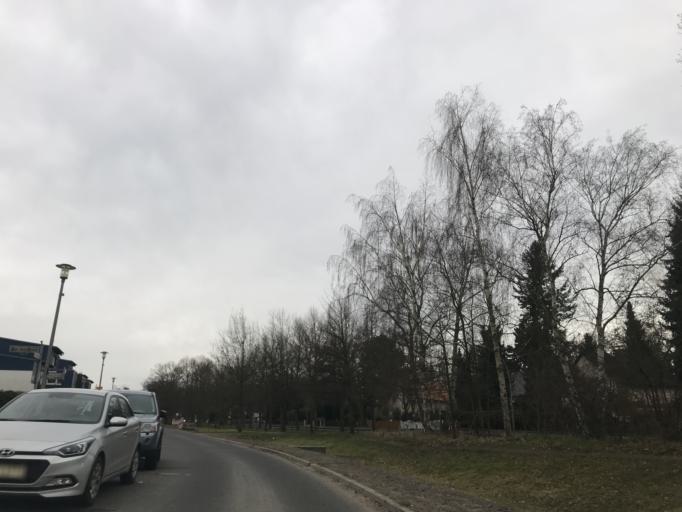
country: DE
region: Berlin
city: Kladow
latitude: 52.4697
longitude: 13.1248
